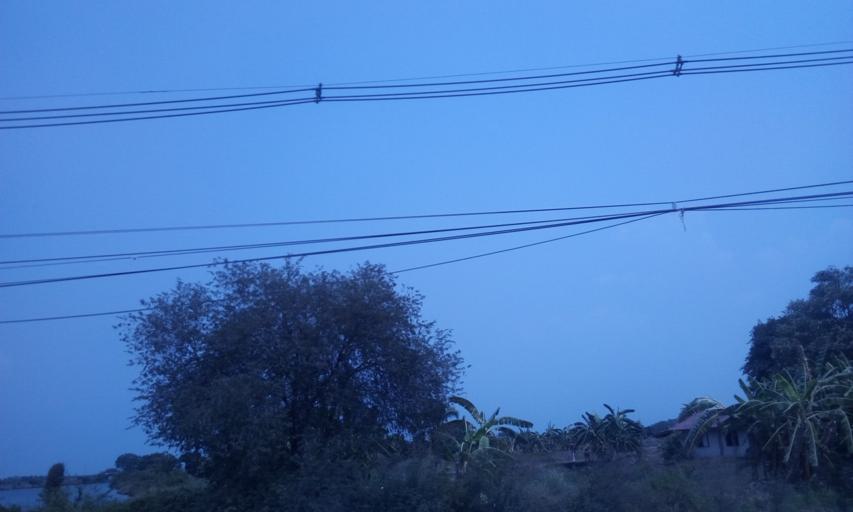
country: TH
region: Chon Buri
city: Phan Thong
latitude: 13.5317
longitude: 101.1503
